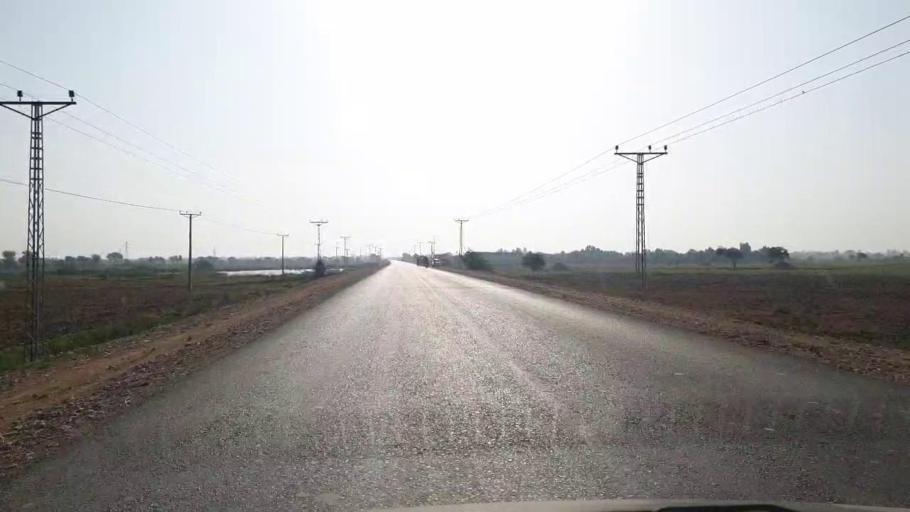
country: PK
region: Sindh
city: Badin
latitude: 24.6734
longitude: 68.8542
